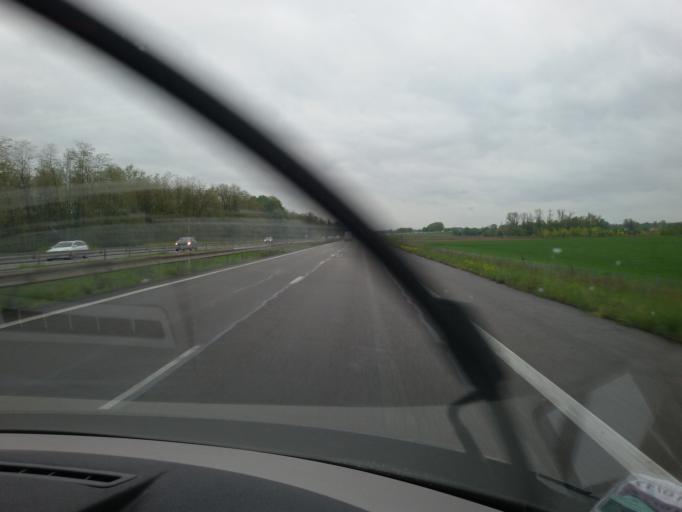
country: FR
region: Rhone-Alpes
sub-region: Departement du Rhone
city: Anse
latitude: 45.9167
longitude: 4.7264
